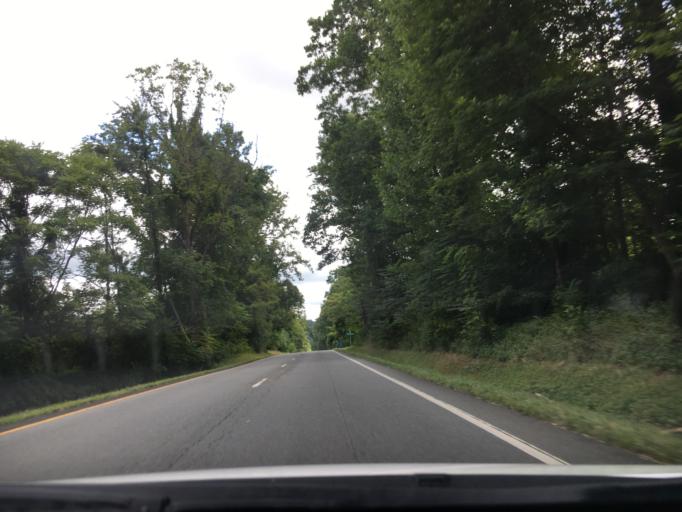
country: US
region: Virginia
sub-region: Nelson County
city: Nellysford
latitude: 37.8765
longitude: -78.7155
